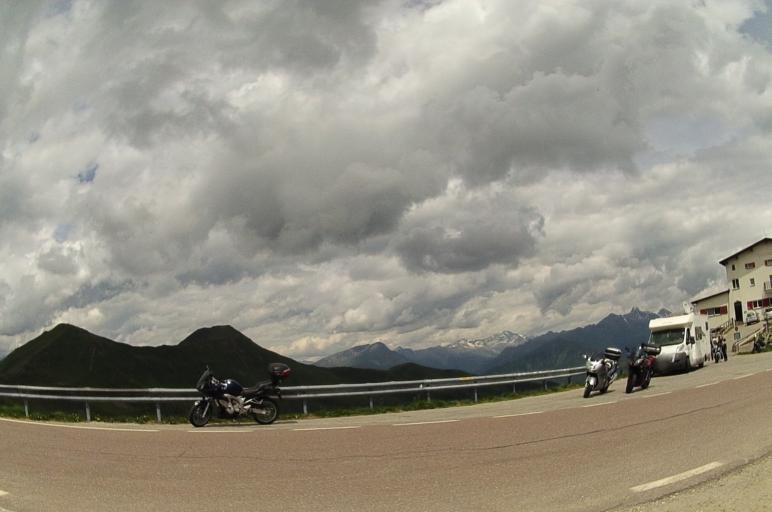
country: IT
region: Trentino-Alto Adige
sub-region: Bolzano
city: Campo di Trens
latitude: 46.8188
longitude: 11.4409
